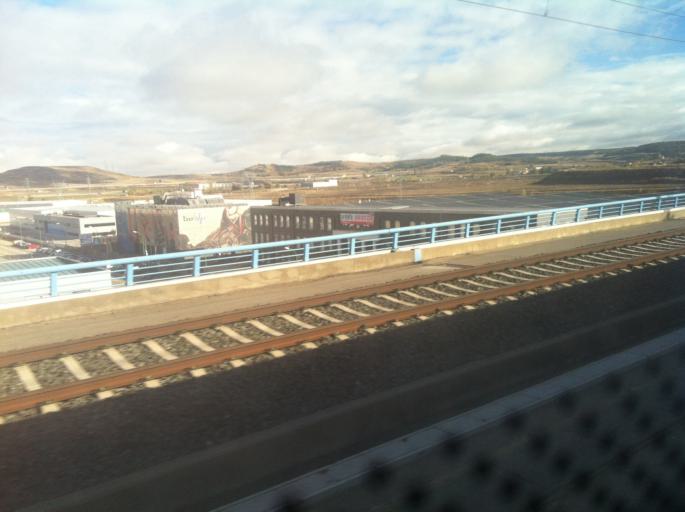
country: ES
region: Castille and Leon
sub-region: Provincia de Burgos
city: Burgos
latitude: 42.3684
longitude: -3.7120
